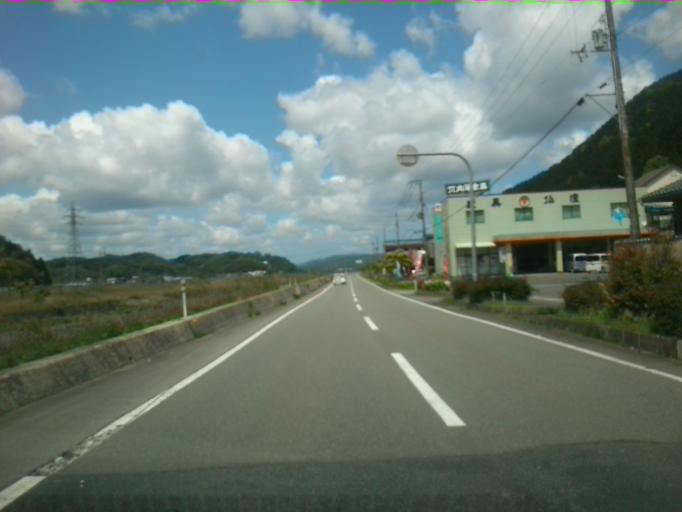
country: JP
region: Hyogo
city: Toyooka
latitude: 35.4484
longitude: 134.8728
